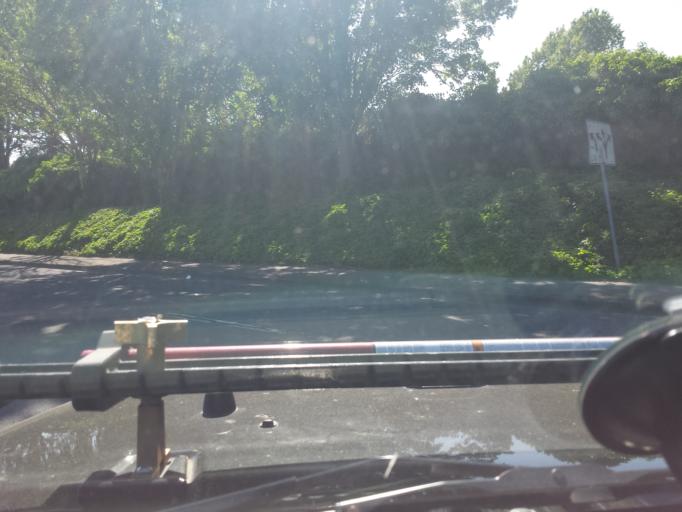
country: US
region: Washington
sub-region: Clark County
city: Walnut Grove
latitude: 45.6526
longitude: -122.5877
